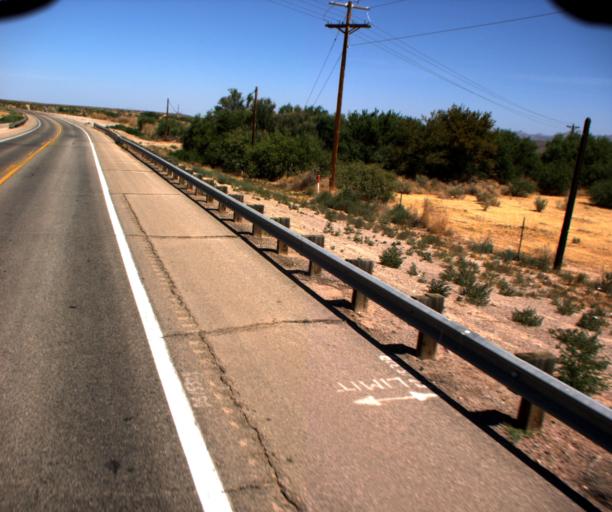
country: US
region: Arizona
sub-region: Graham County
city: Bylas
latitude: 33.0704
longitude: -110.0179
